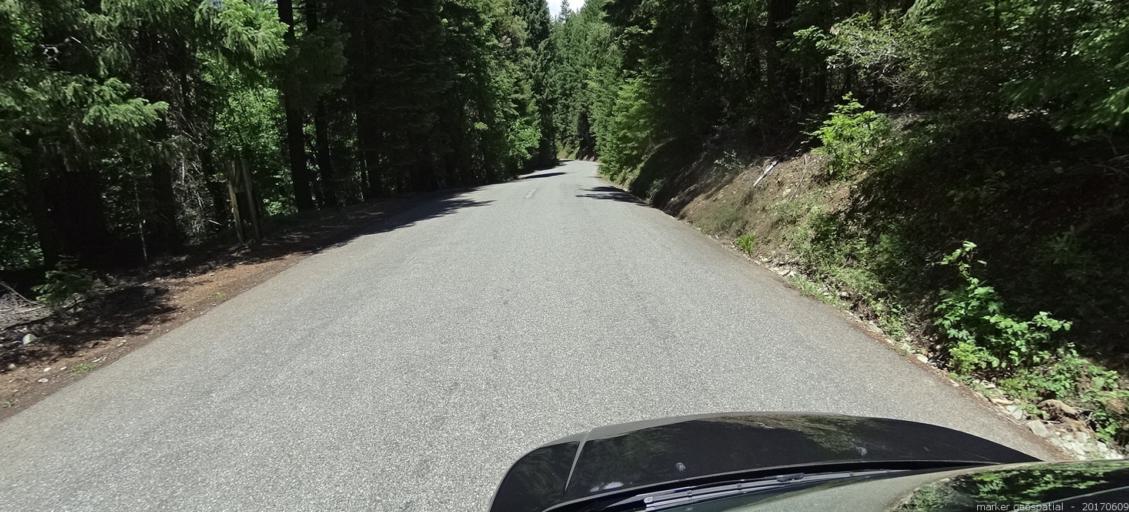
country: US
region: California
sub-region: Siskiyou County
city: Yreka
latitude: 41.3743
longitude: -123.0200
